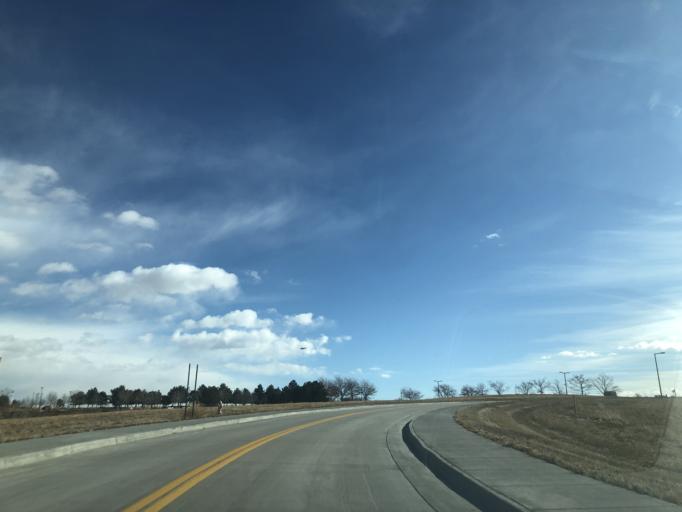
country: US
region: Colorado
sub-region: Douglas County
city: Meridian
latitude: 39.5497
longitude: -104.8596
